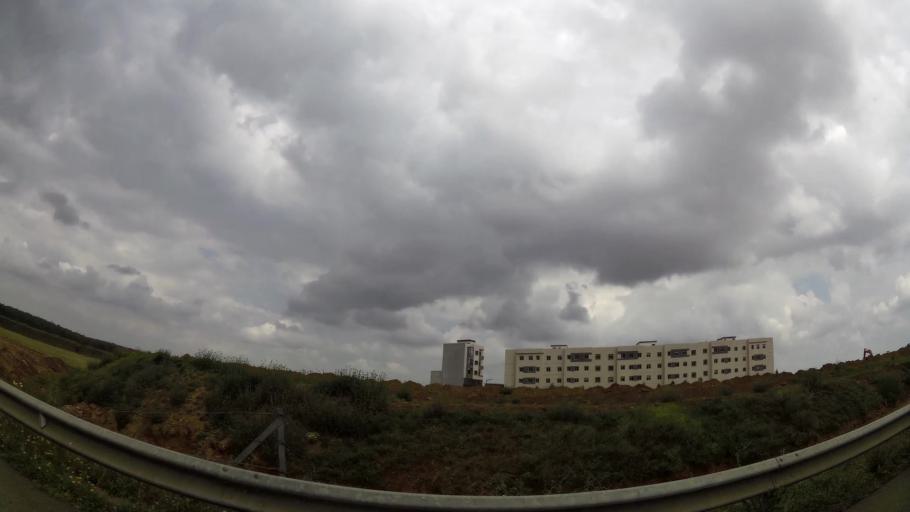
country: MA
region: Rabat-Sale-Zemmour-Zaer
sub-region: Khemisset
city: Tiflet
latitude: 33.8797
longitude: -6.3233
